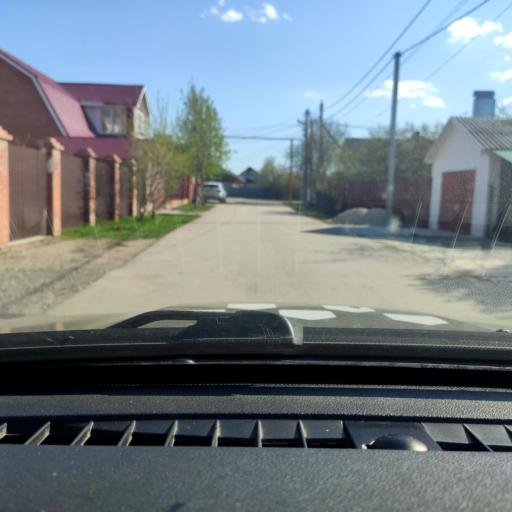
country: RU
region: Samara
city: Tol'yatti
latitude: 53.5626
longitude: 49.3781
